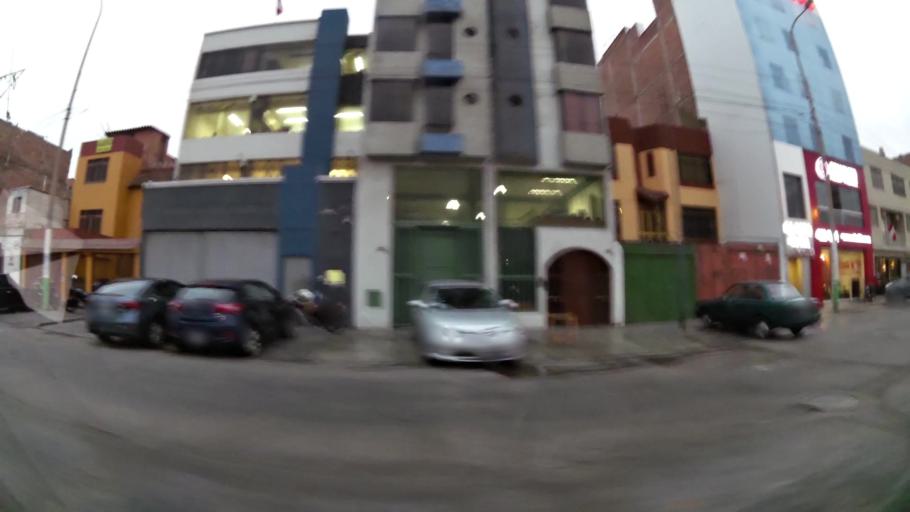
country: PE
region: Callao
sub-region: Callao
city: Callao
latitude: -12.0716
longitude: -77.1108
